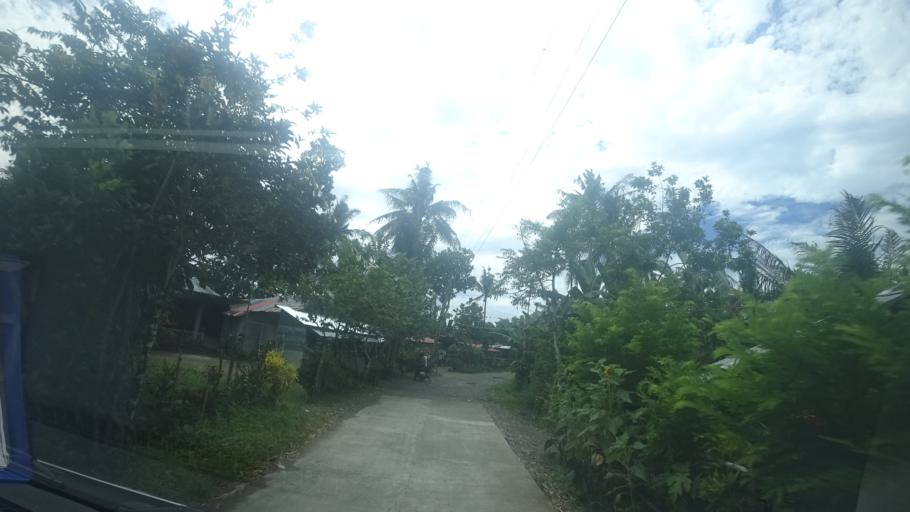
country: PH
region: Eastern Visayas
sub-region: Province of Leyte
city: MacArthur
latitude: 10.8325
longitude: 124.9919
